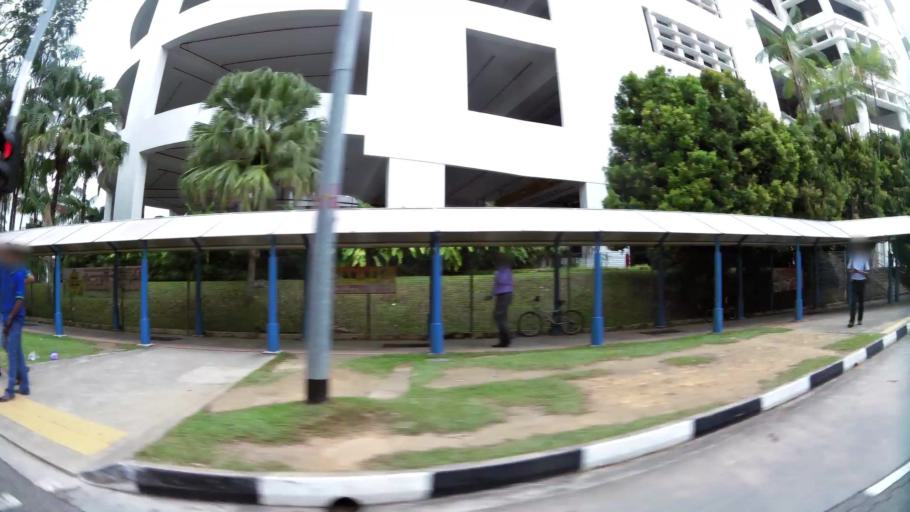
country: MY
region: Johor
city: Kampung Pasir Gudang Baru
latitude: 1.4389
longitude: 103.8402
